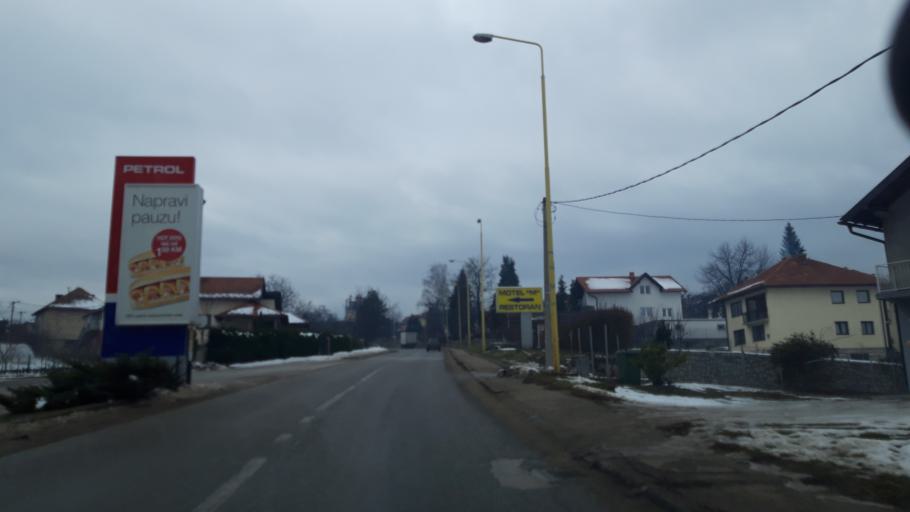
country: BA
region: Republika Srpska
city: Vlasenica
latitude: 44.1821
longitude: 18.9491
